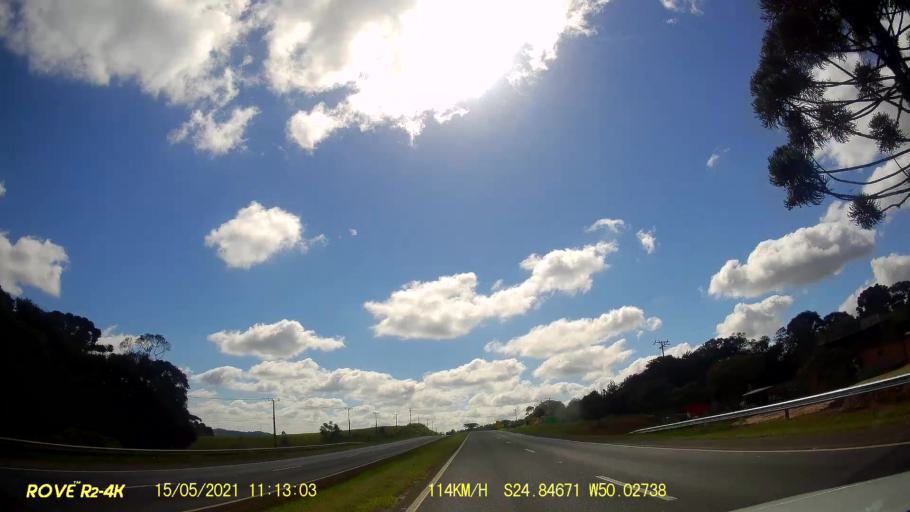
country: BR
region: Parana
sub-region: Castro
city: Castro
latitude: -24.8470
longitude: -50.0274
